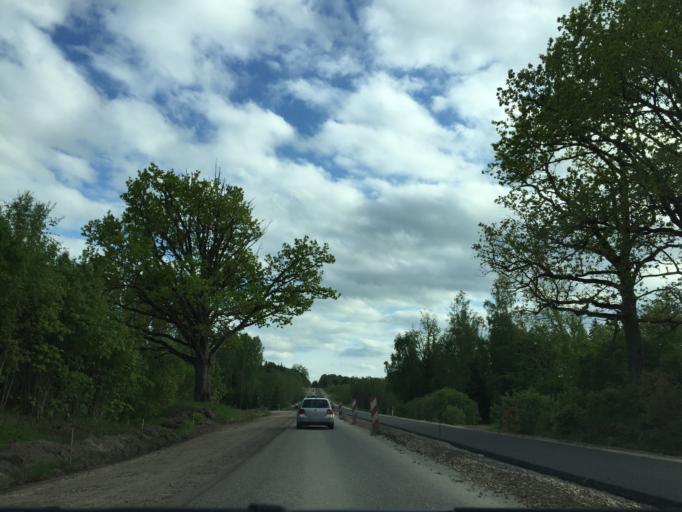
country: LV
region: Amatas Novads
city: Drabesi
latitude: 57.2508
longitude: 25.2613
